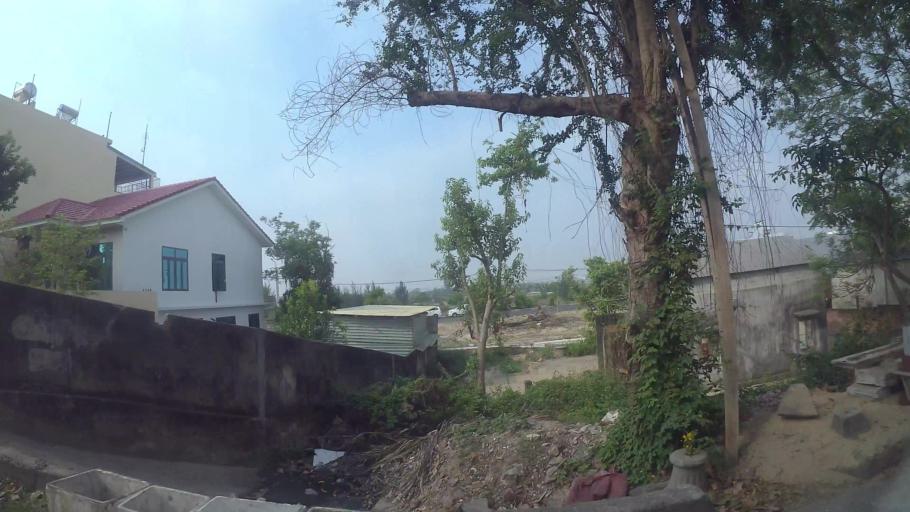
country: VN
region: Da Nang
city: Ngu Hanh Son
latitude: 16.0199
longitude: 108.2486
